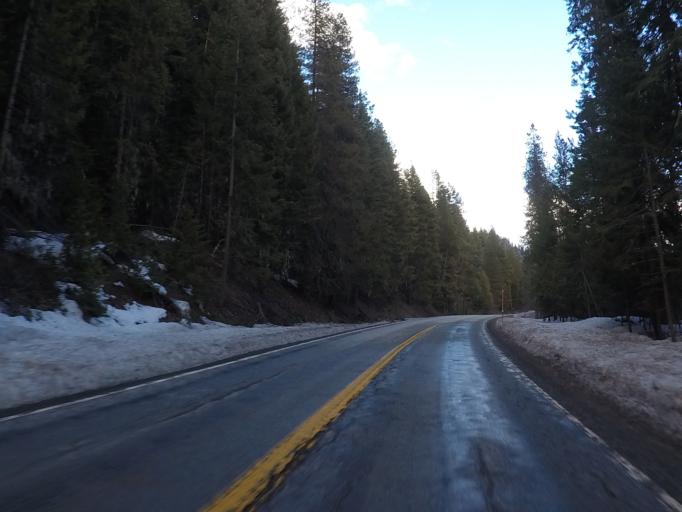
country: US
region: Montana
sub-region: Ravalli County
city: Hamilton
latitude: 46.5167
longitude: -114.7558
